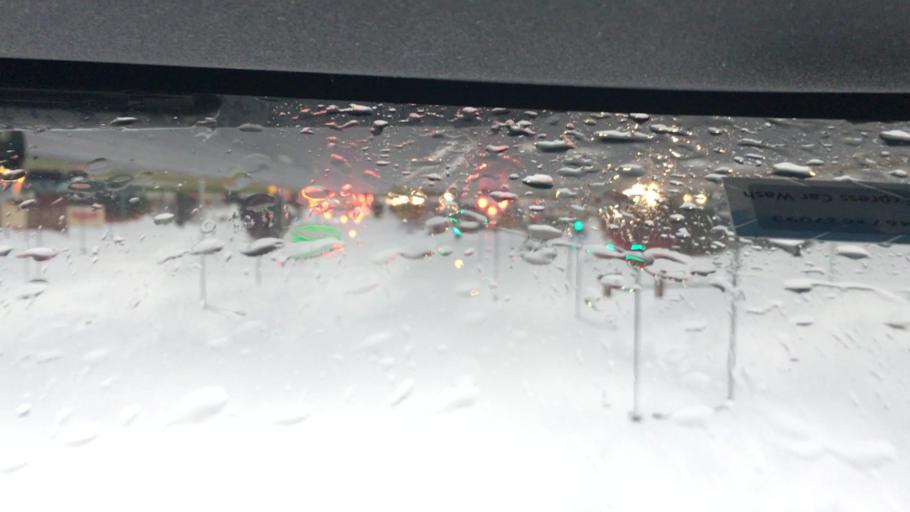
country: US
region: Illinois
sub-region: McLean County
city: Bloomington
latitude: 40.4882
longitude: -88.9555
